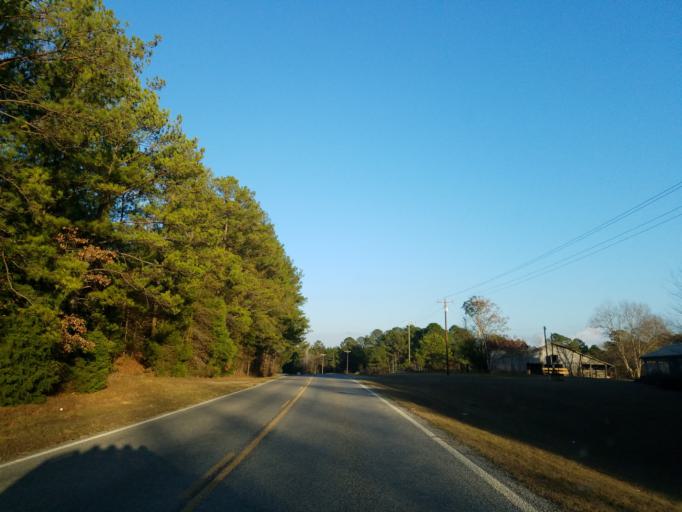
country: US
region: Mississippi
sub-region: Clarke County
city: Stonewall
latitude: 32.1677
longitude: -88.8481
